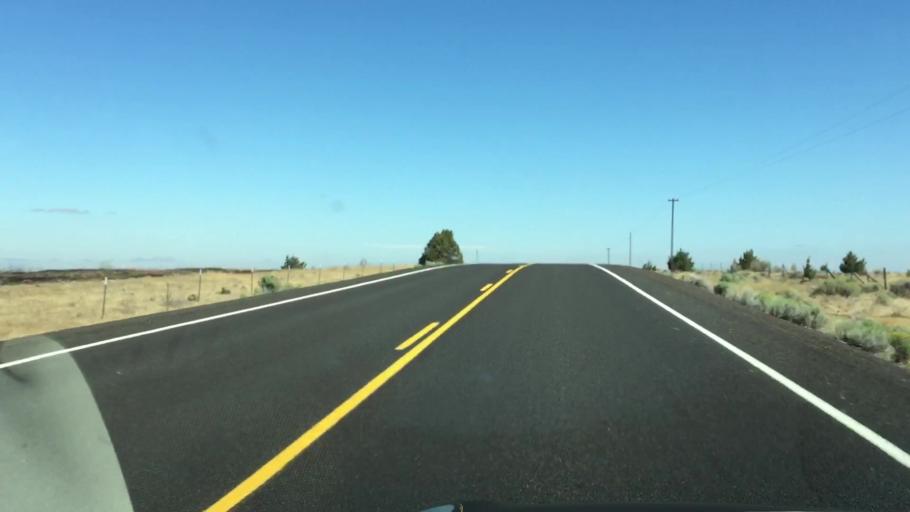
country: US
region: Oregon
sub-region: Jefferson County
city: Warm Springs
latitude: 45.0301
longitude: -120.9939
